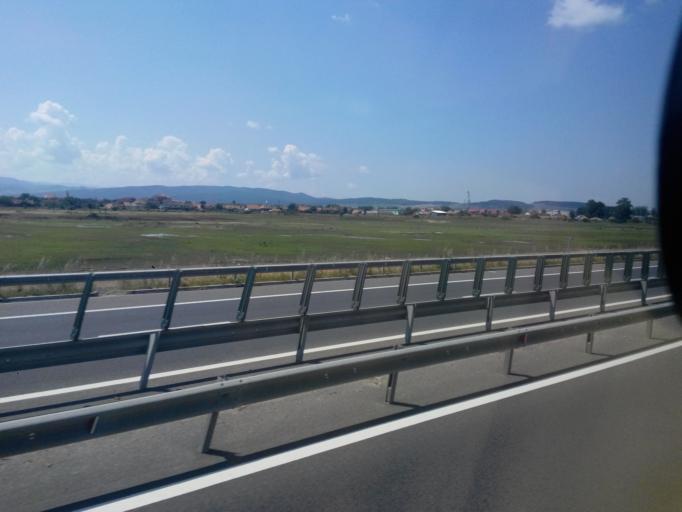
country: RO
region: Alba
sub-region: Municipiul Sebes
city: Sebes
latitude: 45.9724
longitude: 23.5741
